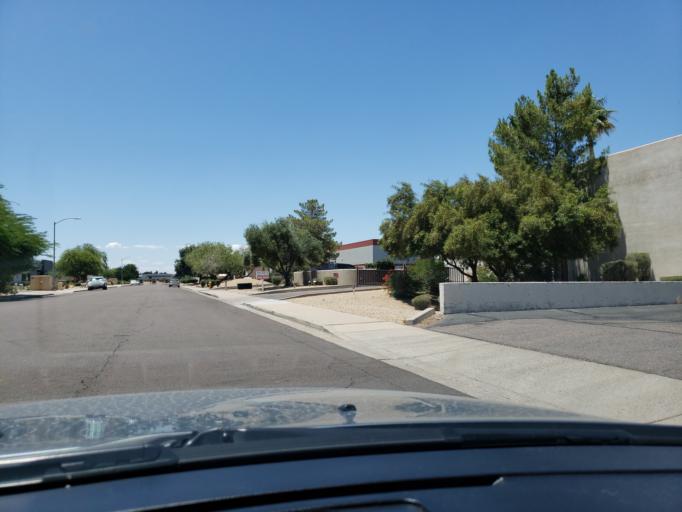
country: US
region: Arizona
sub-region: Maricopa County
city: Paradise Valley
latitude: 33.6165
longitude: -111.9129
